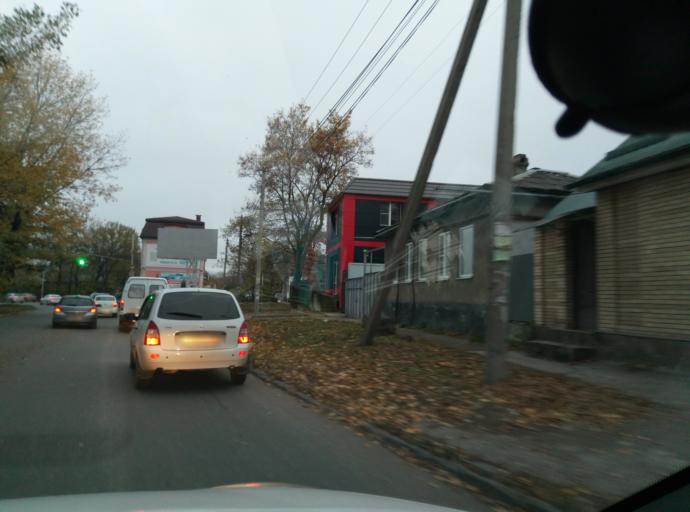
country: RU
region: Stavropol'skiy
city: Yessentuki
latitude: 44.0393
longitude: 42.8651
